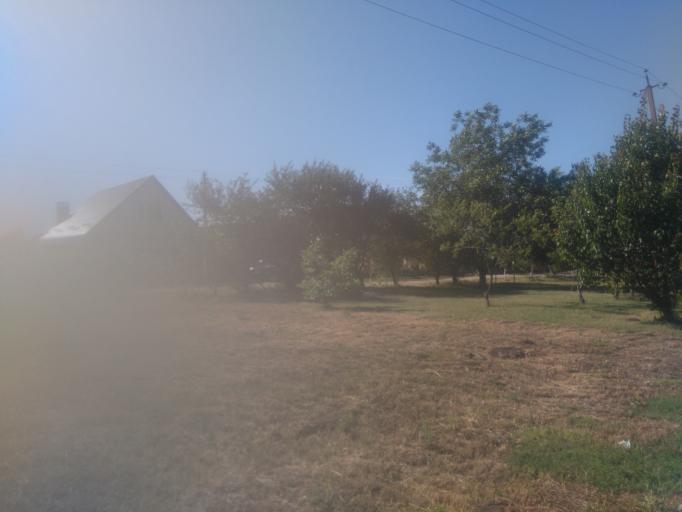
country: RU
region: Krasnodarskiy
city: Fastovetskaya
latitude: 45.9075
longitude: 40.1509
